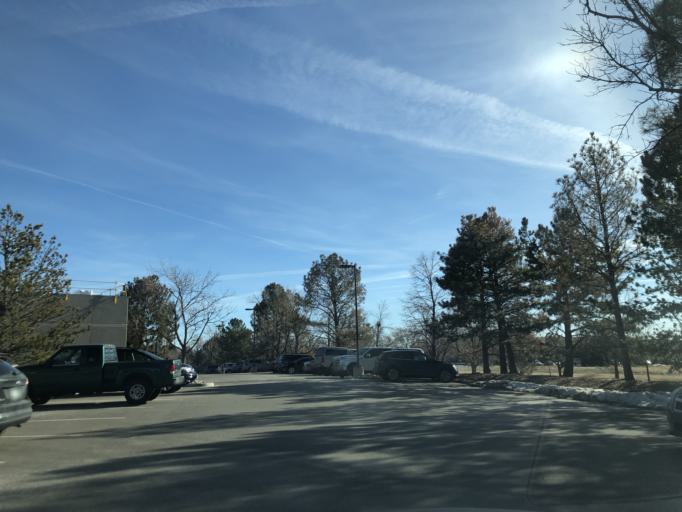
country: US
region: Colorado
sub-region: Adams County
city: Aurora
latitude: 39.7180
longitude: -104.7997
